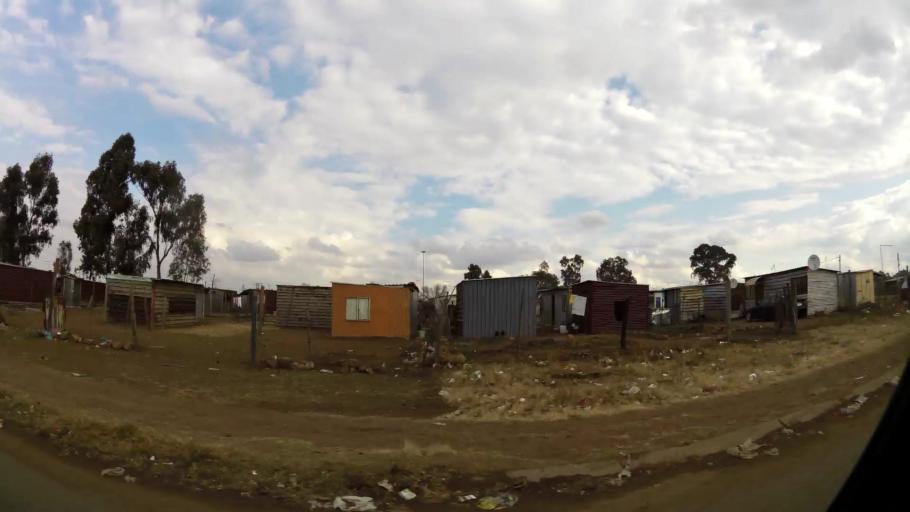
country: ZA
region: Gauteng
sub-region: Sedibeng District Municipality
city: Vanderbijlpark
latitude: -26.6732
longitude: 27.8539
